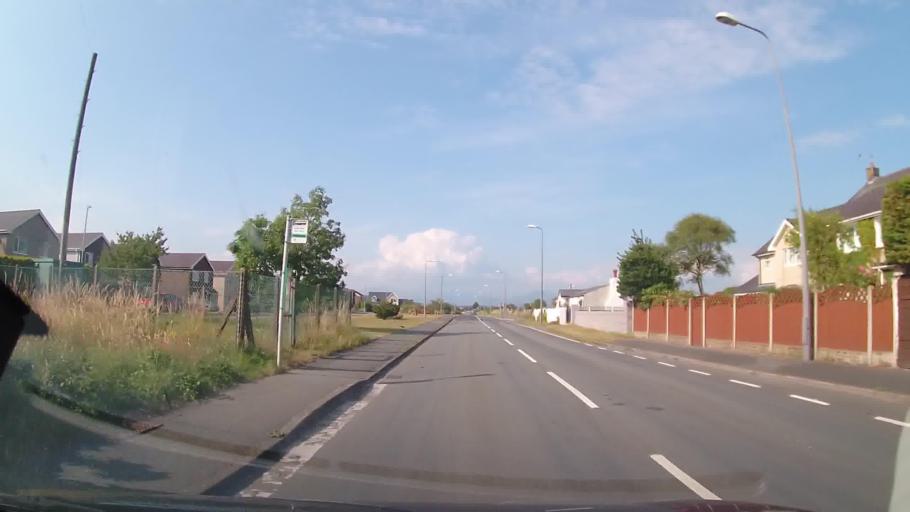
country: GB
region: Wales
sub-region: Gwynedd
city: Llanfair
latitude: 52.8654
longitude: -4.1086
